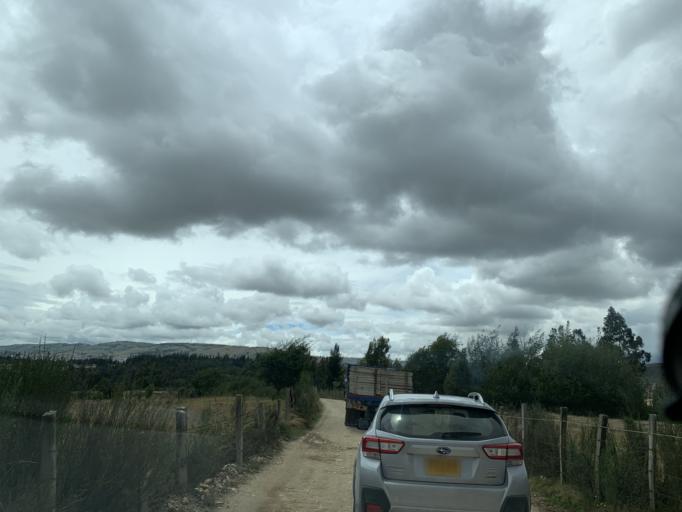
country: CO
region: Boyaca
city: Tunja
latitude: 5.5567
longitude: -73.3297
